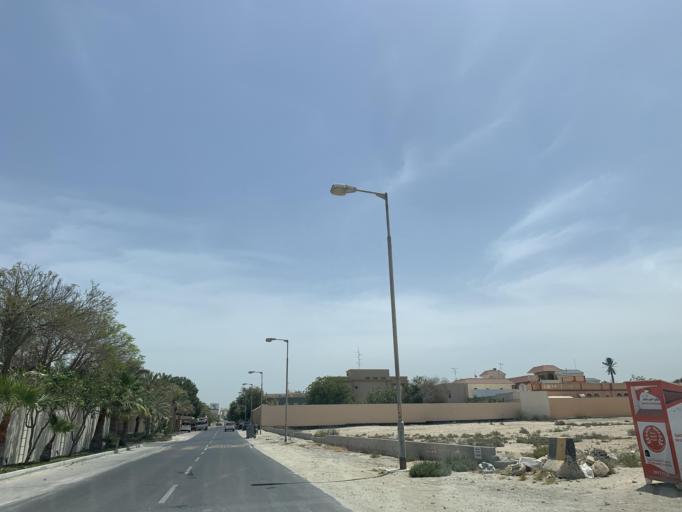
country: BH
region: Northern
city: Ar Rifa'
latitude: 26.1422
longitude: 50.5562
